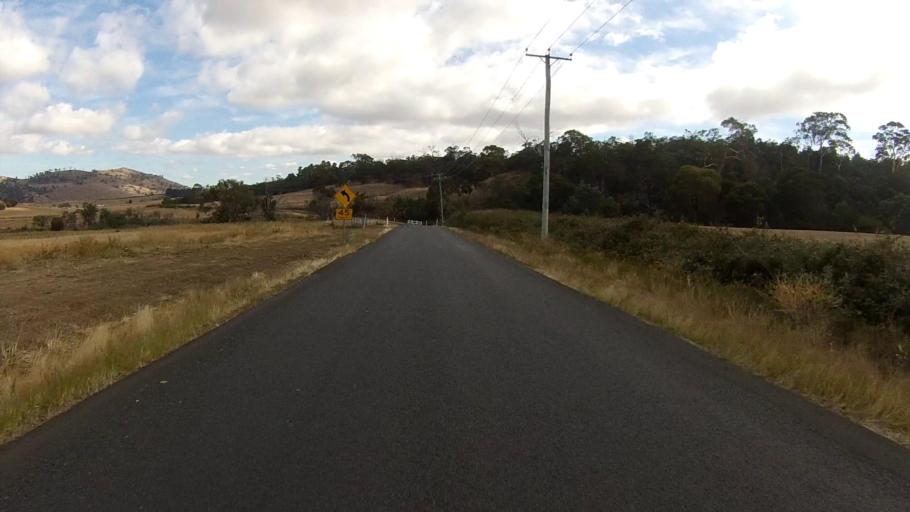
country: AU
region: Tasmania
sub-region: Brighton
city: Old Beach
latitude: -42.7545
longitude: 147.3049
